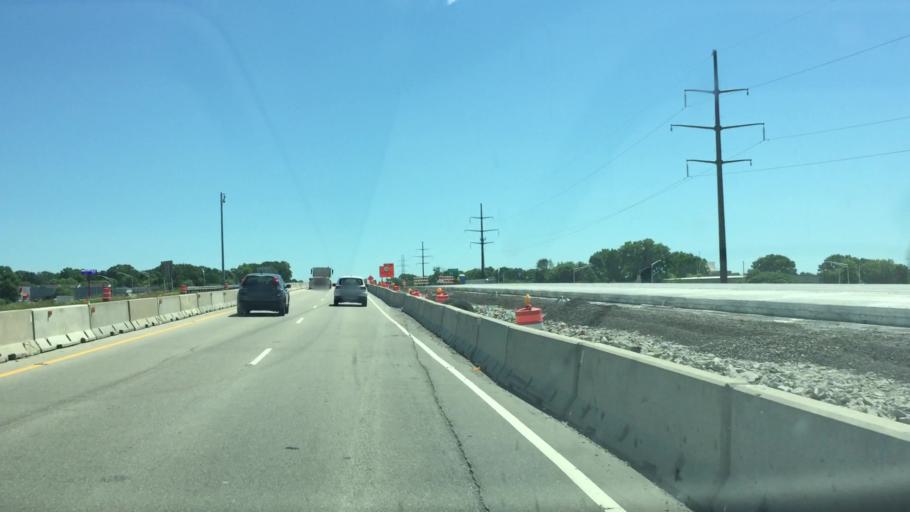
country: US
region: Wisconsin
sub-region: Outagamie County
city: Appleton
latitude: 44.2340
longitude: -88.4263
